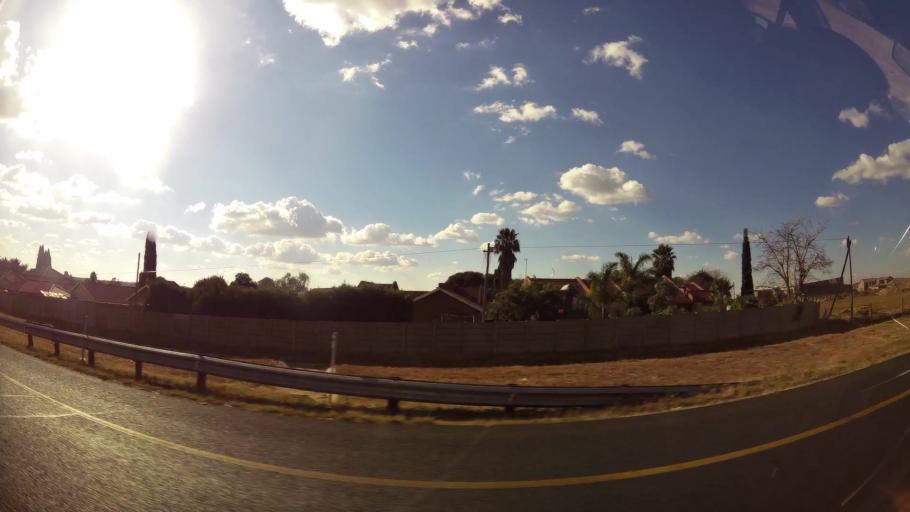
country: ZA
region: Mpumalanga
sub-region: Nkangala District Municipality
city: Witbank
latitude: -25.8956
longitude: 29.2516
